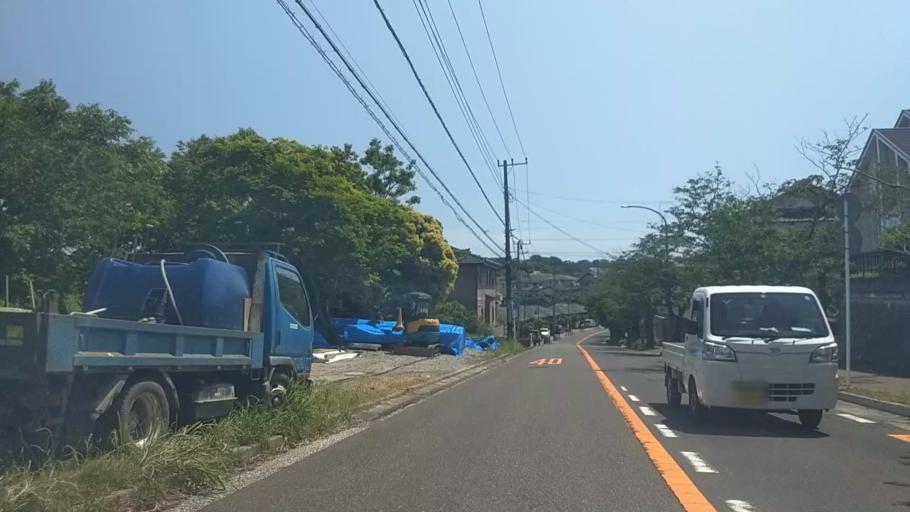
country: JP
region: Kanagawa
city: Zushi
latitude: 35.3107
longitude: 139.5768
